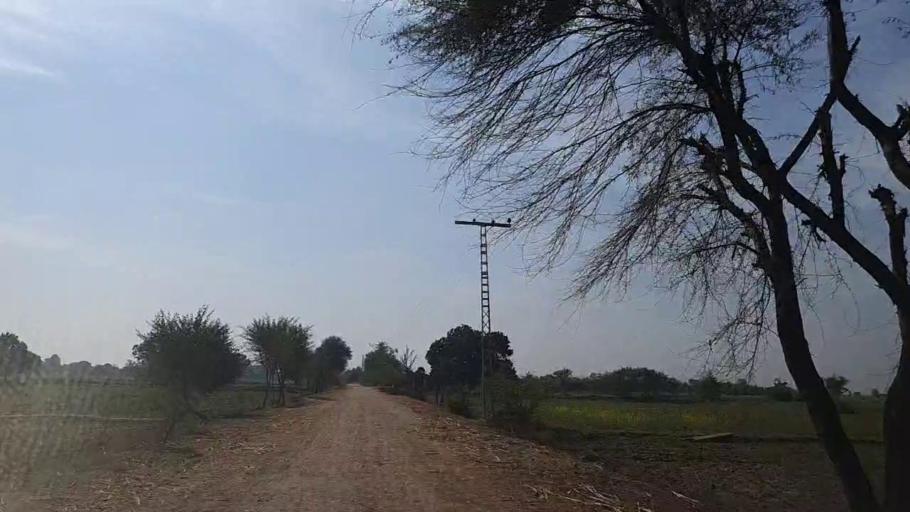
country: PK
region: Sindh
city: Mirpur Khas
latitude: 25.4748
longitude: 68.9745
